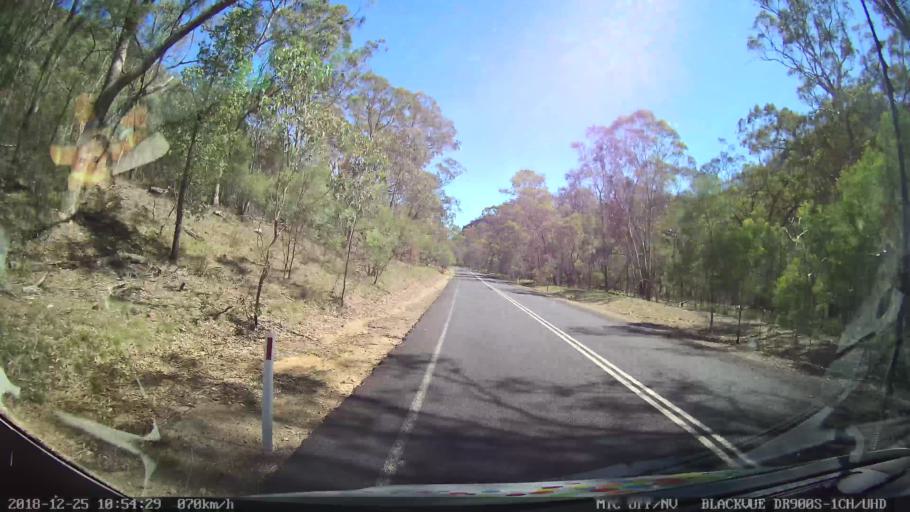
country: AU
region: New South Wales
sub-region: Upper Hunter Shire
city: Merriwa
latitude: -32.4093
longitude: 150.2733
